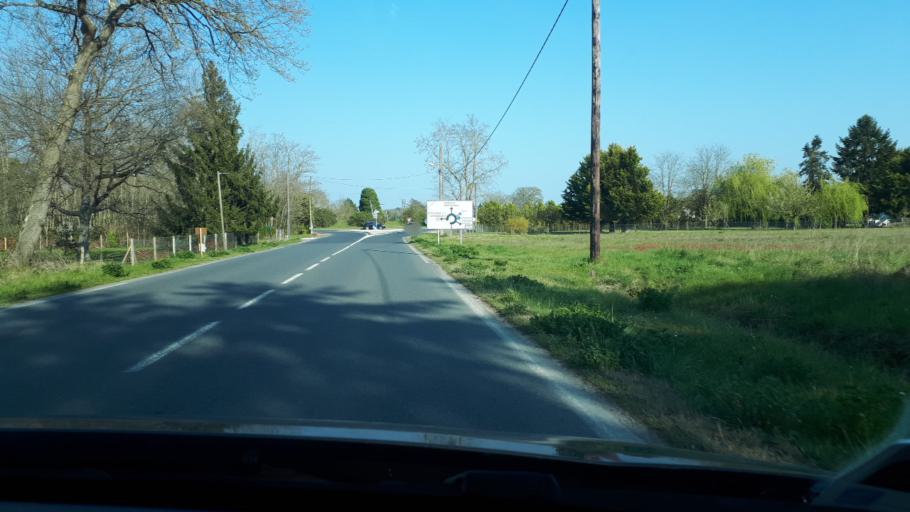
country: FR
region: Centre
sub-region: Departement d'Indre-et-Loire
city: Civray-de-Touraine
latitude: 47.3223
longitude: 1.0329
